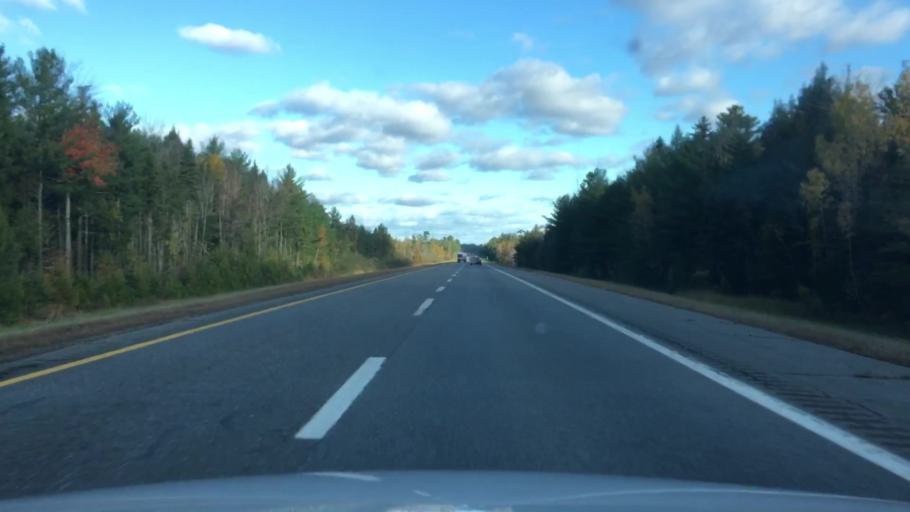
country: US
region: Maine
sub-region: Penobscot County
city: Greenbush
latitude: 45.1269
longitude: -68.6955
